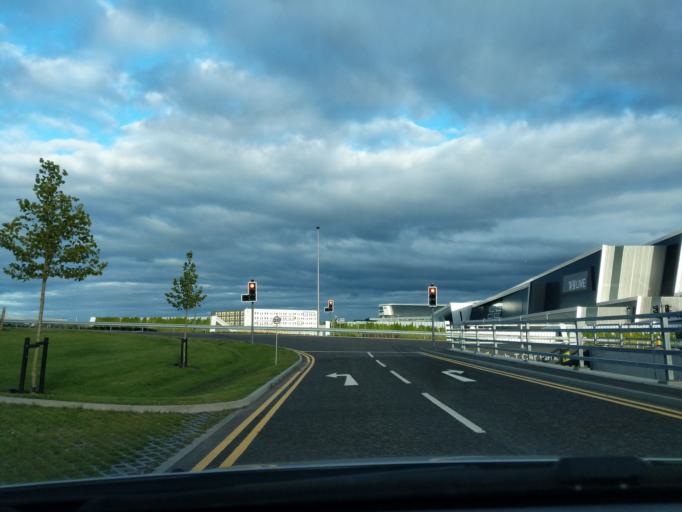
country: GB
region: Scotland
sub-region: Aberdeen City
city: Dyce
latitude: 57.1877
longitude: -2.1946
